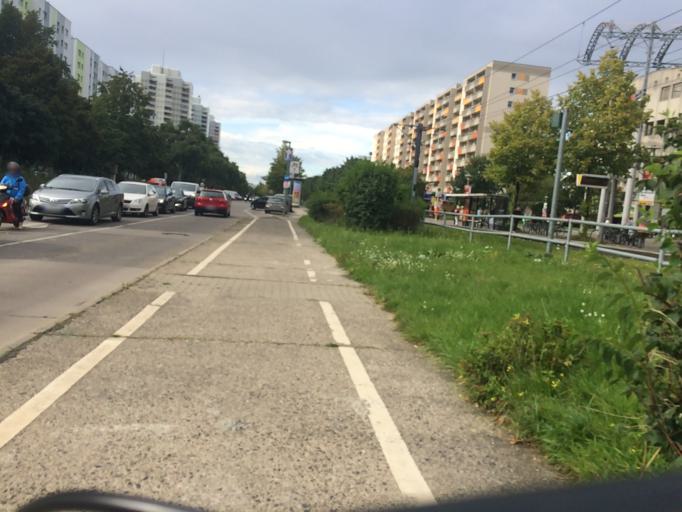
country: DE
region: Berlin
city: Neu-Hohenschoenhausen
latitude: 52.5636
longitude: 13.5047
